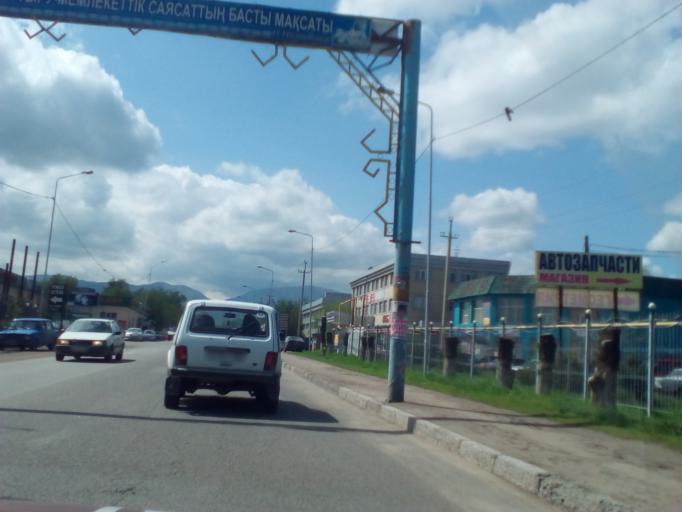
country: KZ
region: Almaty Oblysy
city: Burunday
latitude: 43.2137
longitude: 76.6437
